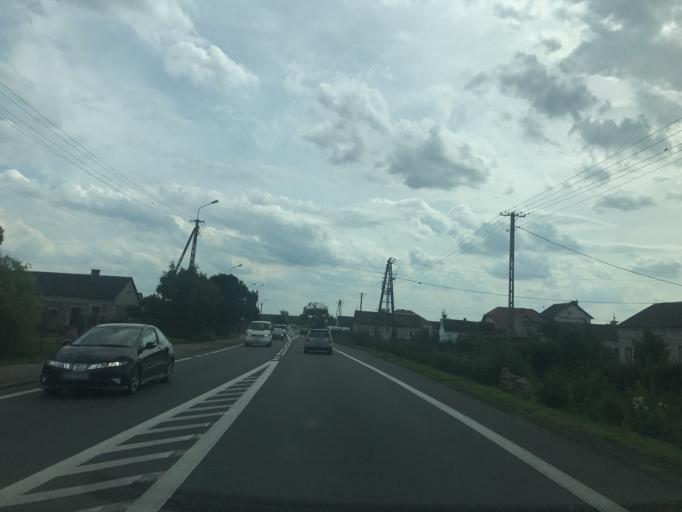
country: PL
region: Masovian Voivodeship
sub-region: Powiat mlawski
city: Strzegowo
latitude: 52.9425
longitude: 20.2820
